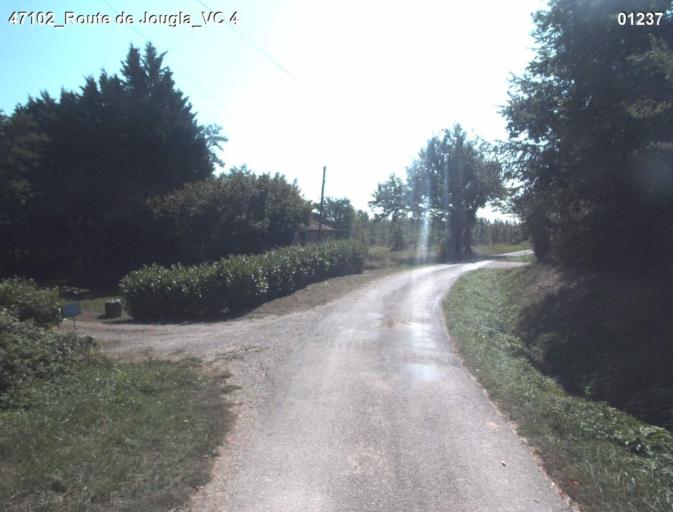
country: FR
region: Aquitaine
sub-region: Departement du Lot-et-Garonne
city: Laplume
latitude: 44.0542
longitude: 0.4392
